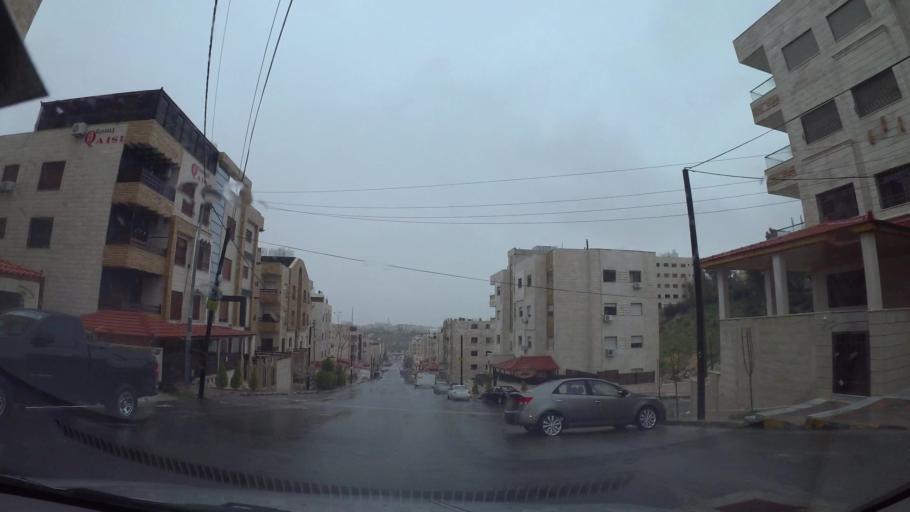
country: JO
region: Amman
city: Al Jubayhah
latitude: 32.0317
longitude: 35.8882
